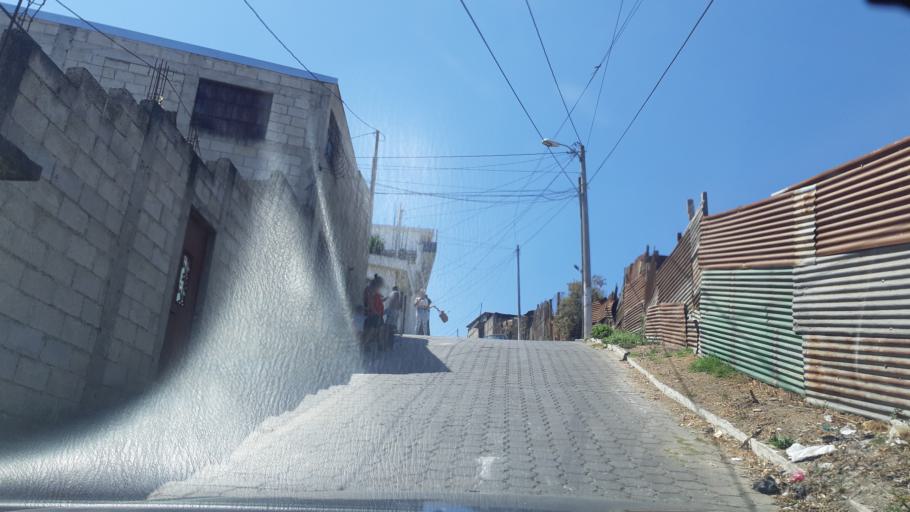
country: GT
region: Chimaltenango
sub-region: Municipio de Chimaltenango
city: Chimaltenango
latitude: 14.6567
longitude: -90.8167
